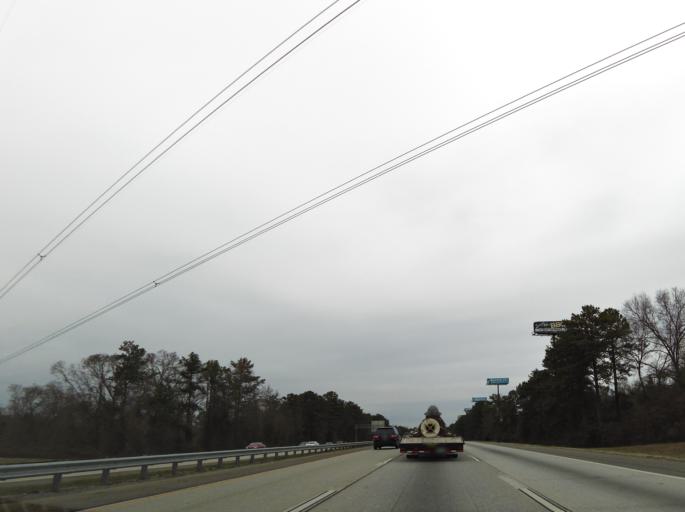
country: US
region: Georgia
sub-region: Peach County
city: Byron
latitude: 32.6277
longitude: -83.7431
